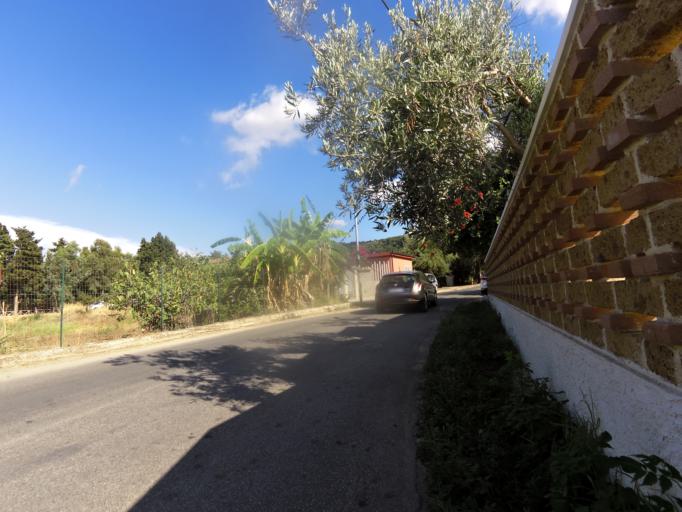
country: IT
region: Calabria
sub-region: Provincia di Vibo-Valentia
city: Santa Domenica
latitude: 38.6688
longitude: 15.8722
